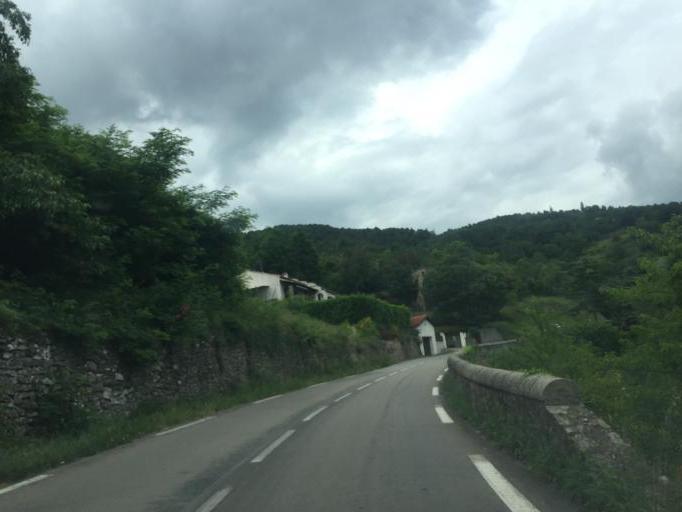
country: FR
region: Rhone-Alpes
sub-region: Departement de l'Ardeche
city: Privas
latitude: 44.7429
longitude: 4.6052
